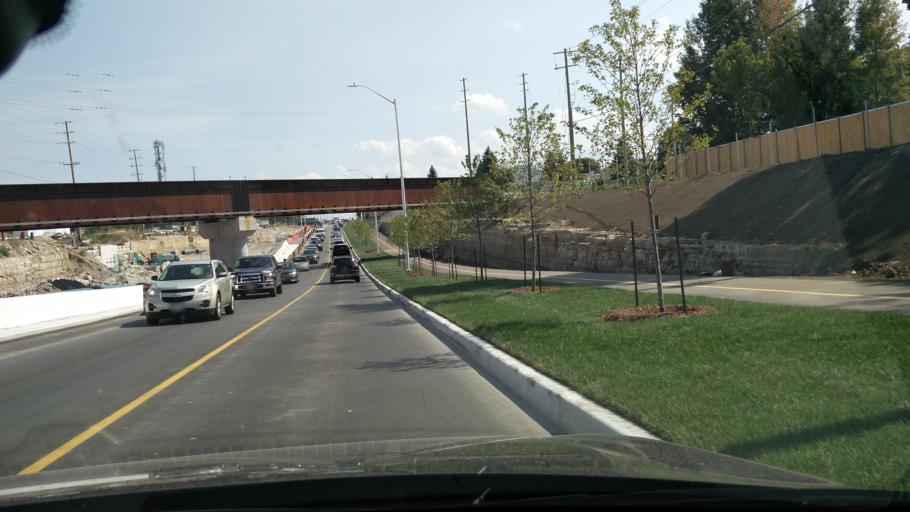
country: CA
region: Ontario
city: Bells Corners
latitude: 45.2802
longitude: -75.7524
